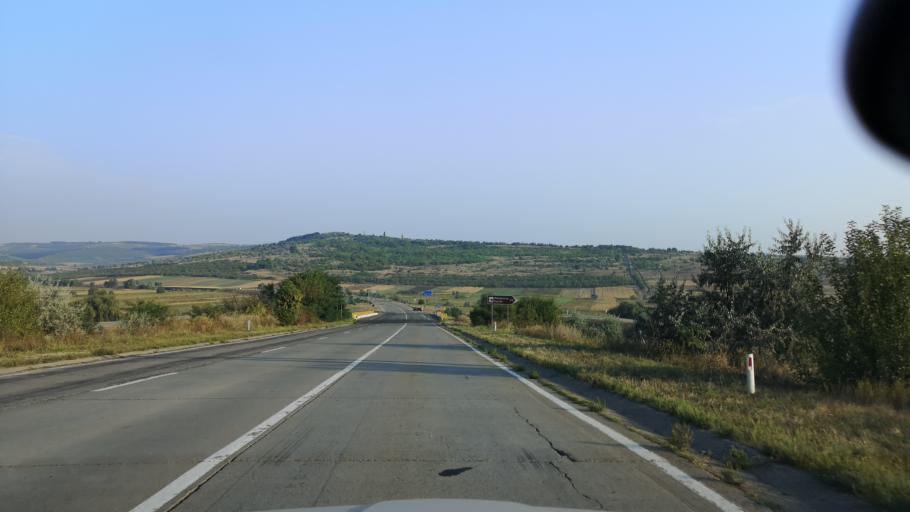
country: MD
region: Taraclia
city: Telenesti
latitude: 47.3787
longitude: 28.4507
